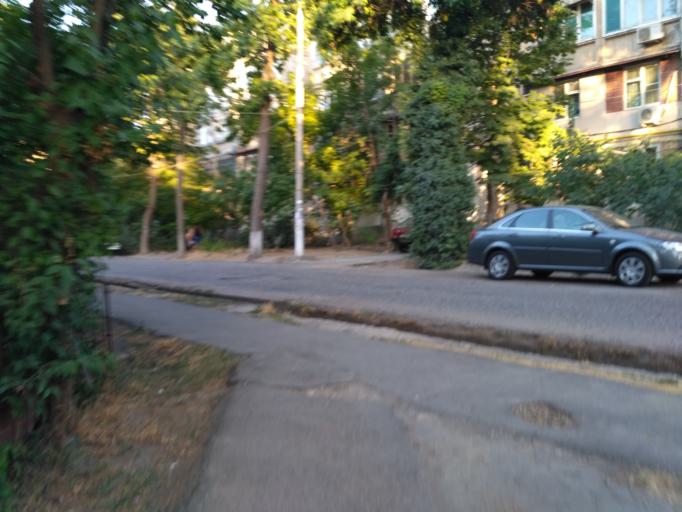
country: UZ
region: Toshkent Shahri
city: Tashkent
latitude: 41.2696
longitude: 69.2780
